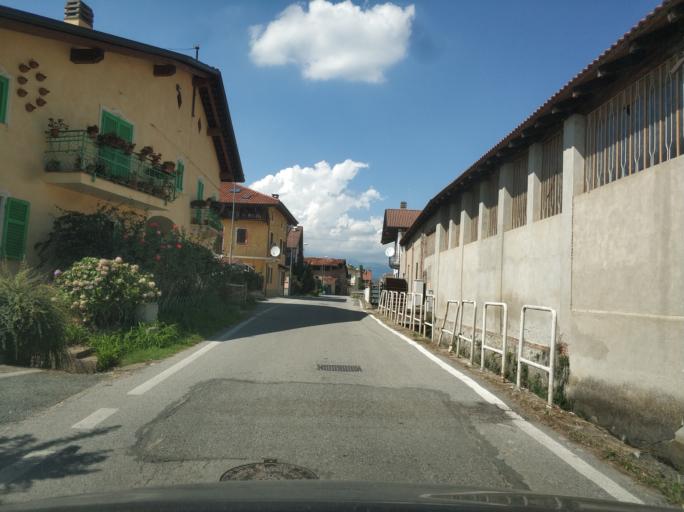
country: IT
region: Piedmont
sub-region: Provincia di Torino
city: Rivarolo Canavese
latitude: 45.3144
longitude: 7.7229
